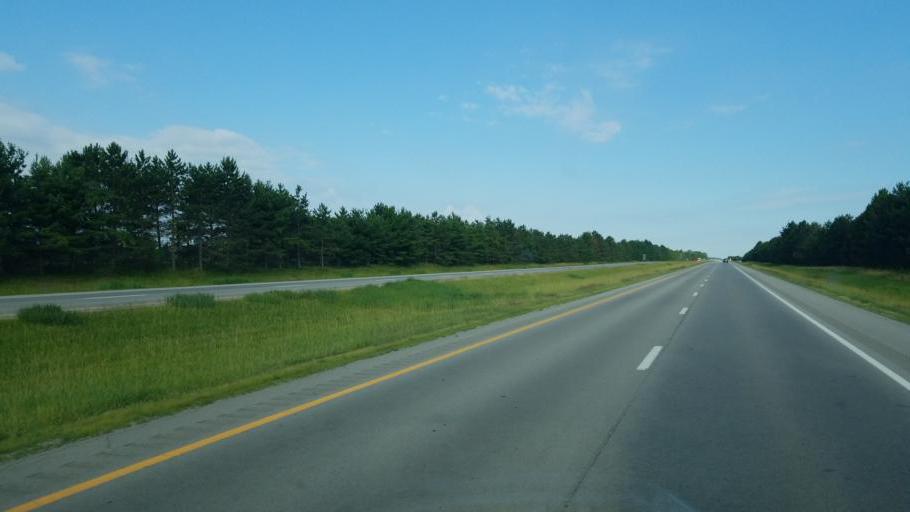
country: US
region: Ohio
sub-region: Wyandot County
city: Carey
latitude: 40.9534
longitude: -83.4341
